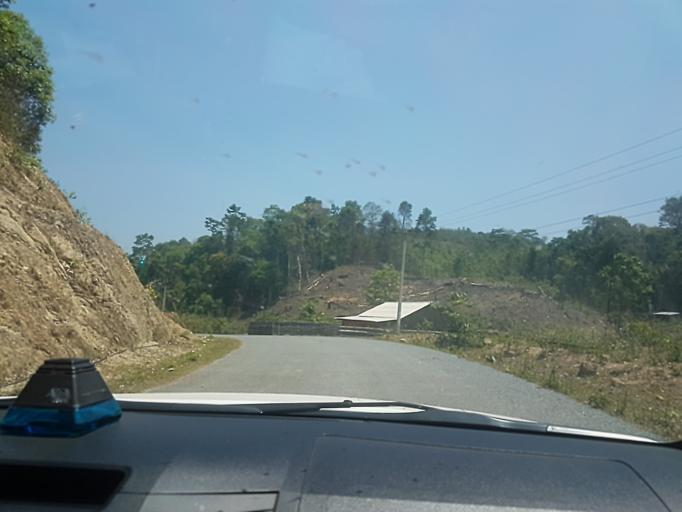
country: VN
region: Nghe An
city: Con Cuong
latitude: 18.5843
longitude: 104.6233
